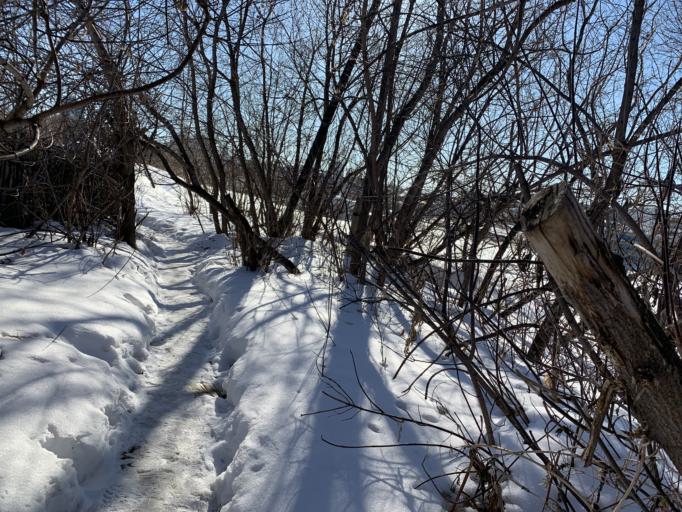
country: RU
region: Chuvashia
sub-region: Cheboksarskiy Rayon
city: Cheboksary
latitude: 56.1475
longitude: 47.2612
